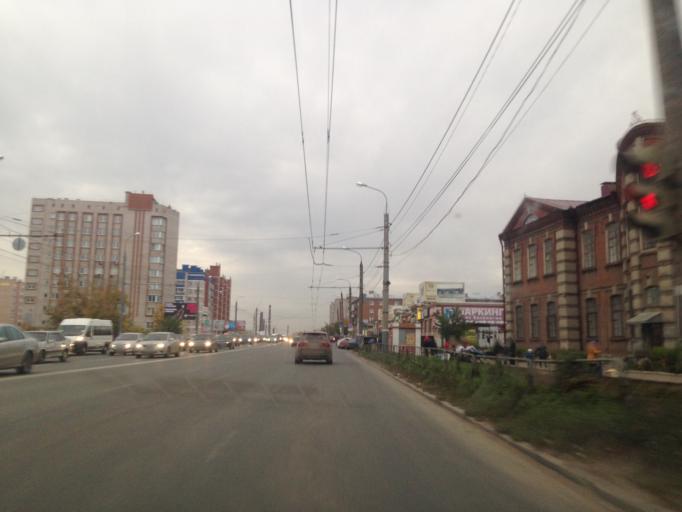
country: RU
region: Udmurtiya
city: Izhevsk
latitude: 56.8378
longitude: 53.2144
